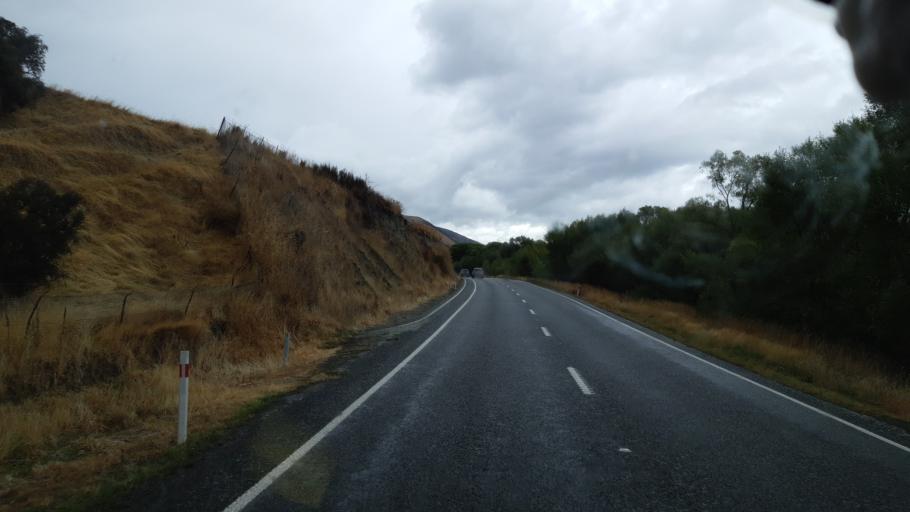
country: NZ
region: Canterbury
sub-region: Hurunui District
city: Amberley
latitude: -42.5784
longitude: 172.7597
